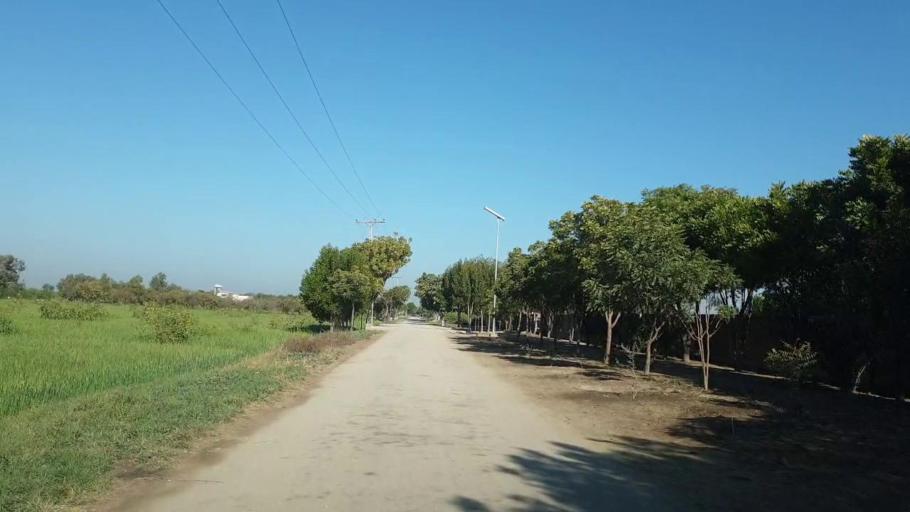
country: PK
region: Sindh
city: Mirpur Khas
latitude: 25.5466
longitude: 69.0411
